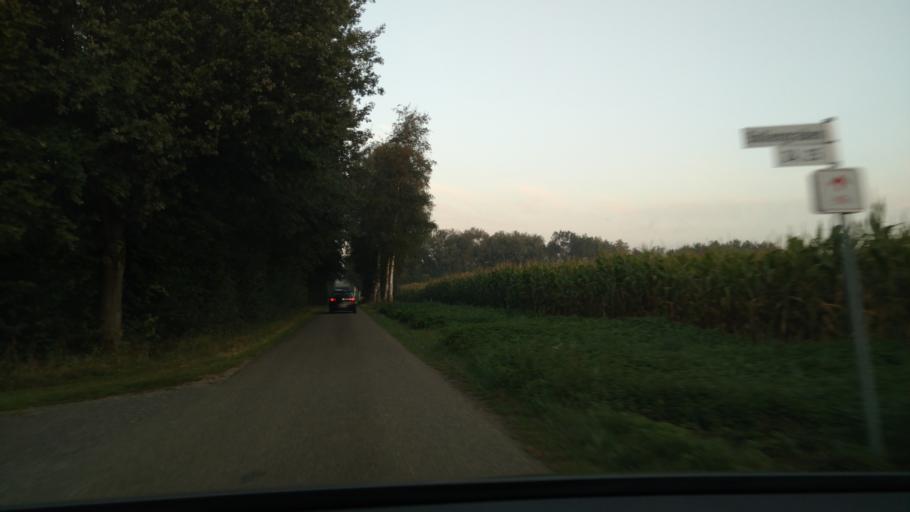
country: DE
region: North Rhine-Westphalia
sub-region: Regierungsbezirk Munster
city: Velen
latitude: 51.8577
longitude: 7.0113
